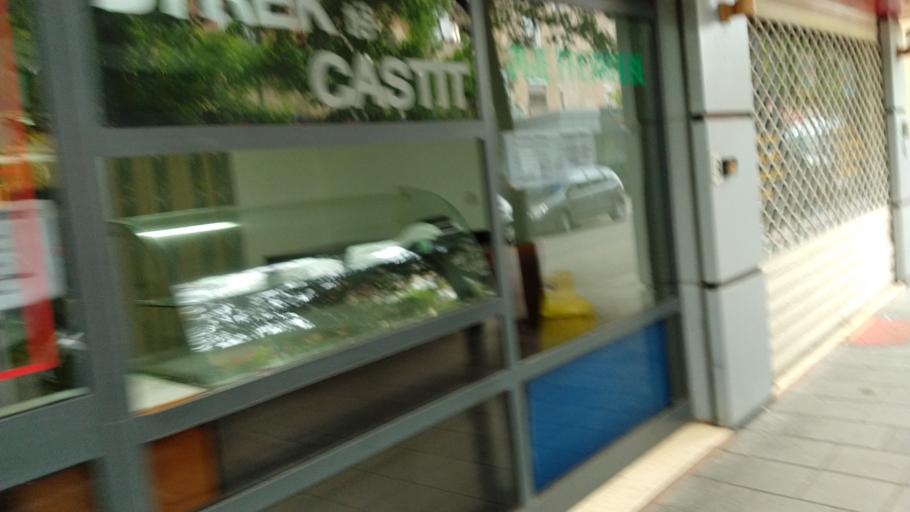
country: AL
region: Tirane
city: Tirana
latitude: 41.3316
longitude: 19.8116
